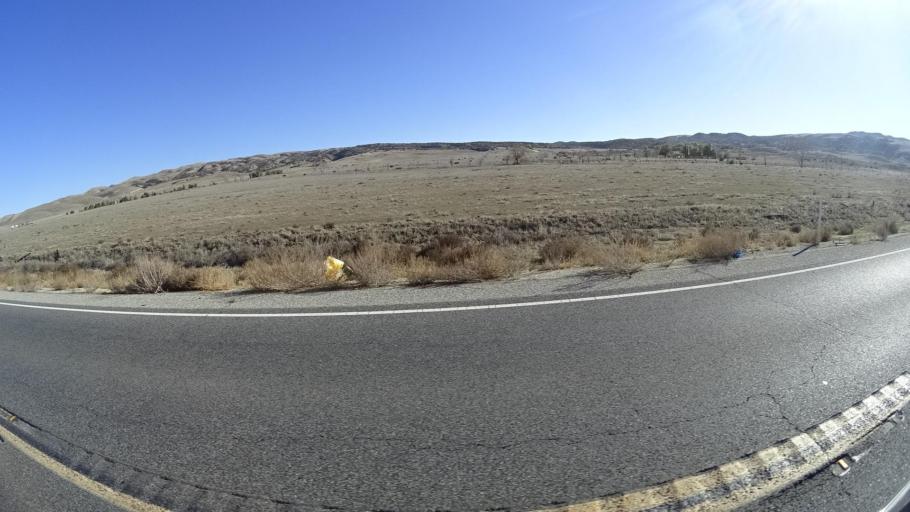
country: US
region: California
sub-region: Kern County
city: Maricopa
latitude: 34.9399
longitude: -119.4669
